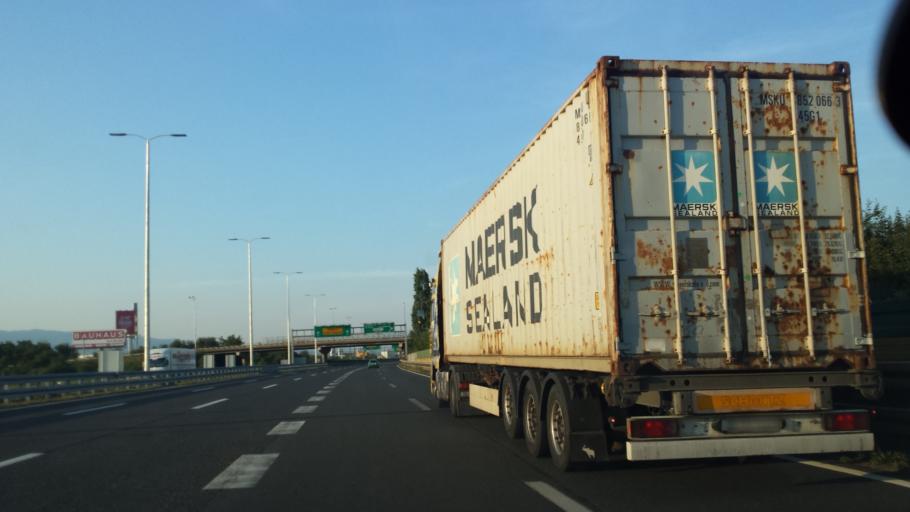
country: HR
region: Grad Zagreb
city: Brezovica
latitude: 45.7506
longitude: 15.8859
